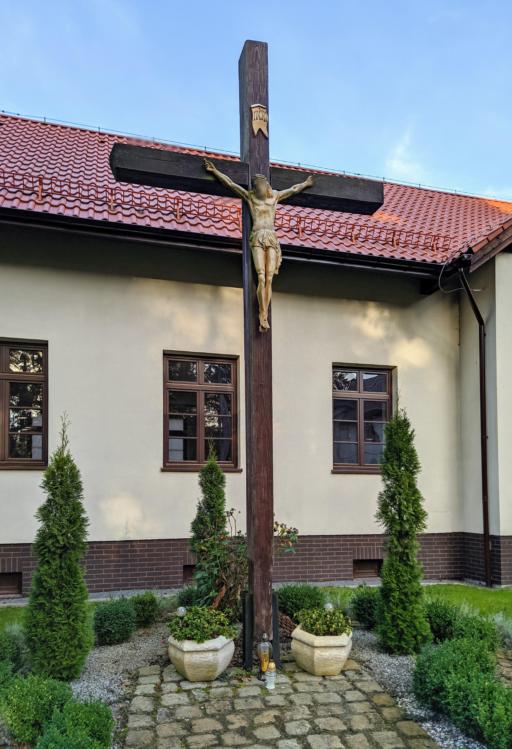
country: PL
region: Lubusz
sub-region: Powiat swiebodzinski
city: Sieniawa
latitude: 52.4104
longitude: 15.4750
